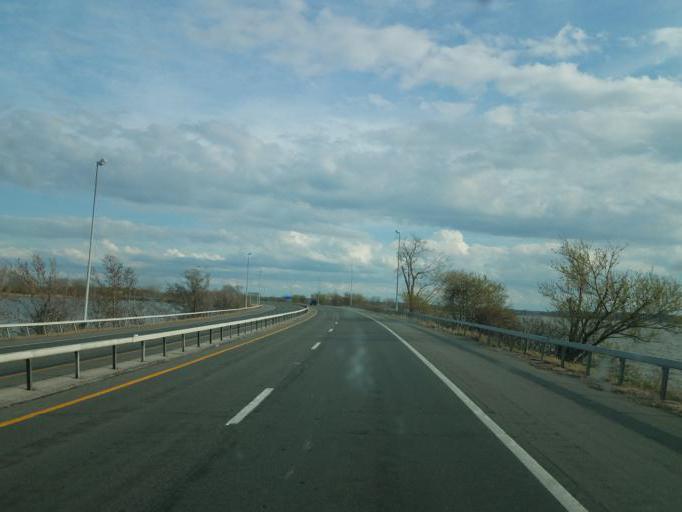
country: US
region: Ohio
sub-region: Ottawa County
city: Port Clinton
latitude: 41.4685
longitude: -82.8331
